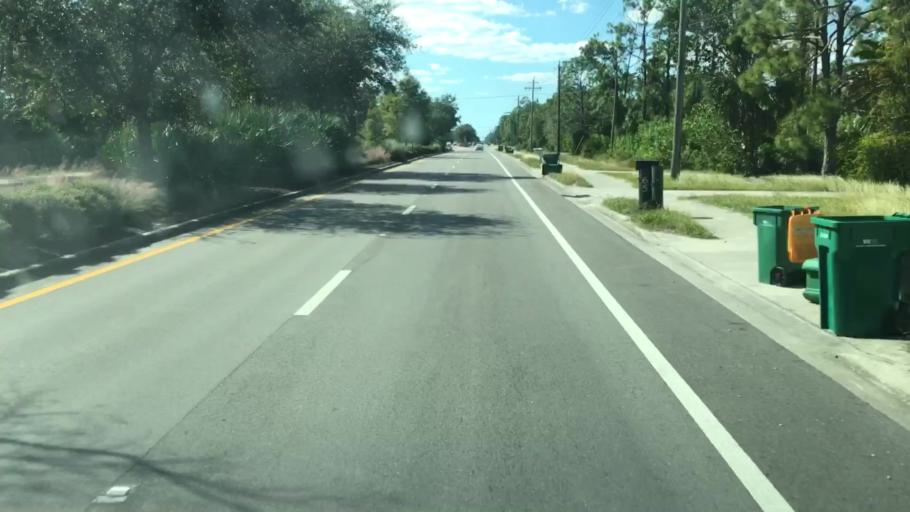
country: US
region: Florida
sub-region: Collier County
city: Orangetree
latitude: 26.2299
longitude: -81.6100
